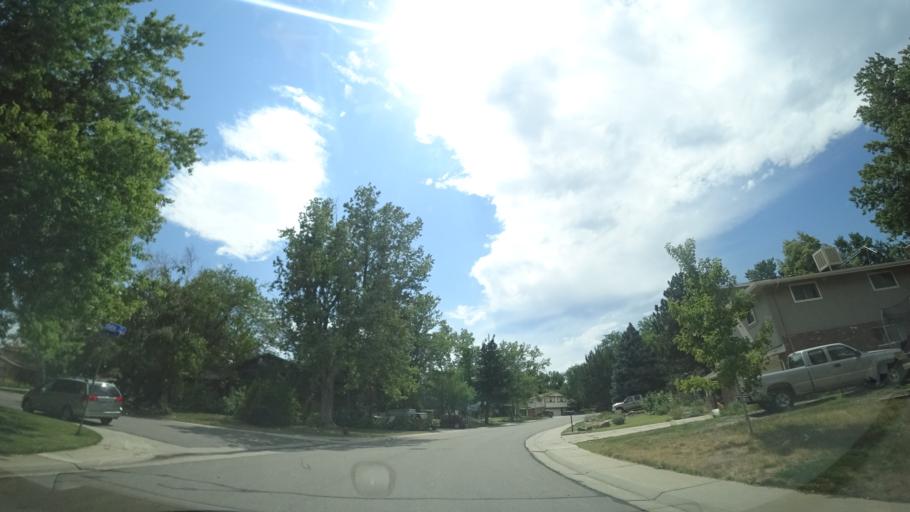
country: US
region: Colorado
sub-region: Jefferson County
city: Lakewood
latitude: 39.6902
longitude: -105.1123
